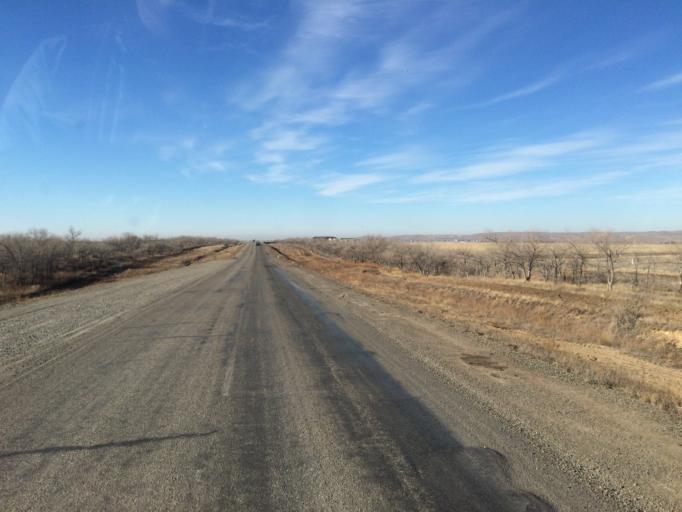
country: KZ
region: Aqtoebe
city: Aqtobe
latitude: 50.2930
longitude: 57.6240
